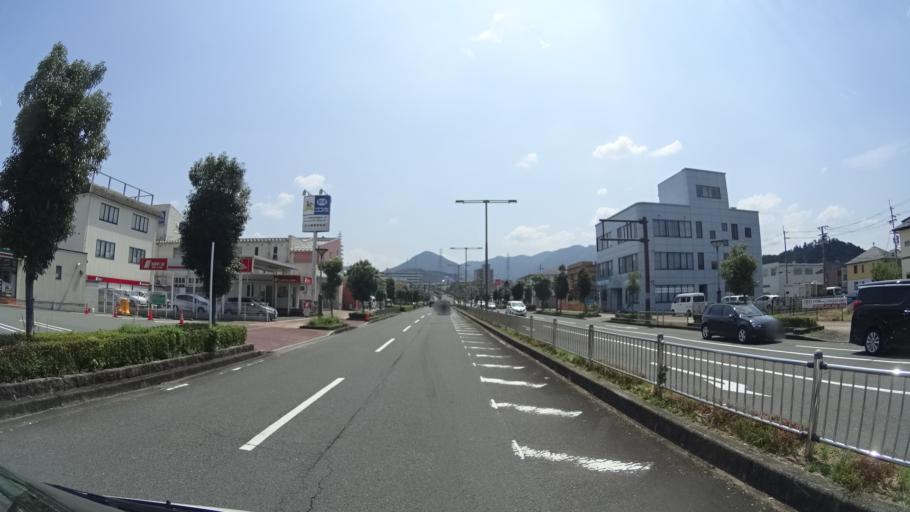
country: JP
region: Kyoto
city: Fukuchiyama
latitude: 35.2948
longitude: 135.1181
